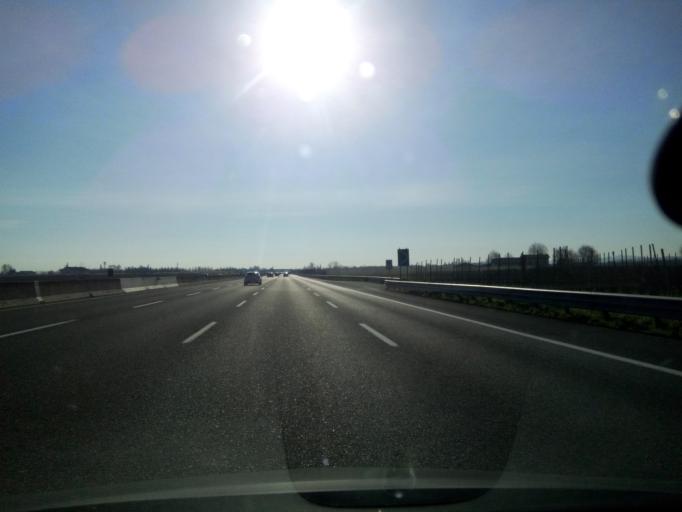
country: IT
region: Emilia-Romagna
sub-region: Provincia di Modena
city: San Cesario sul Panaro
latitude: 44.5710
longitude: 11.0138
